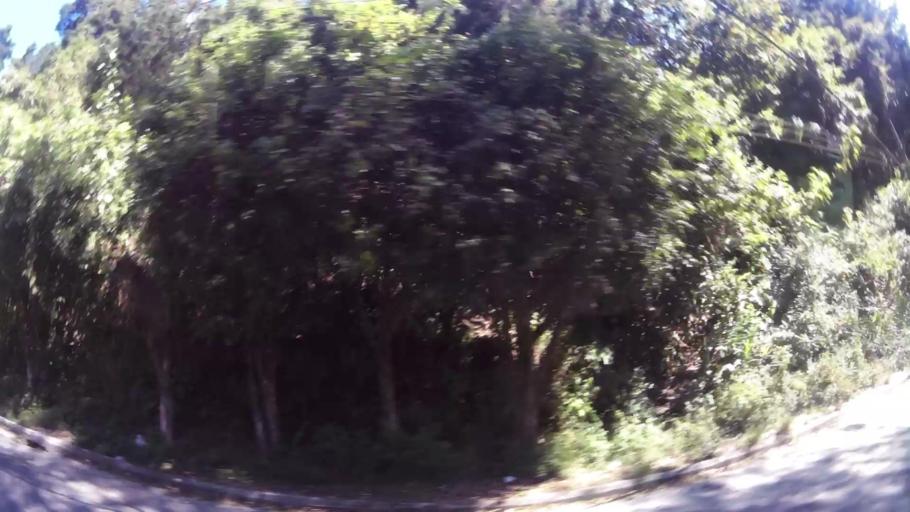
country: GT
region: Guatemala
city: Petapa
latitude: 14.4926
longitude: -90.5486
